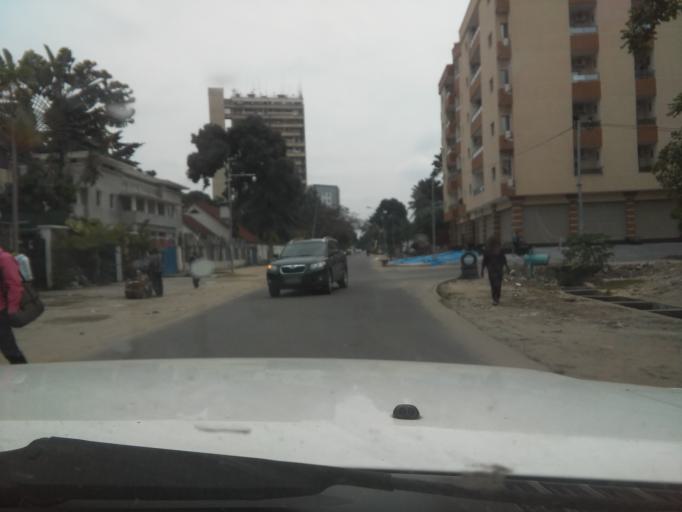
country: CD
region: Kinshasa
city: Kinshasa
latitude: -4.3145
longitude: 15.2868
